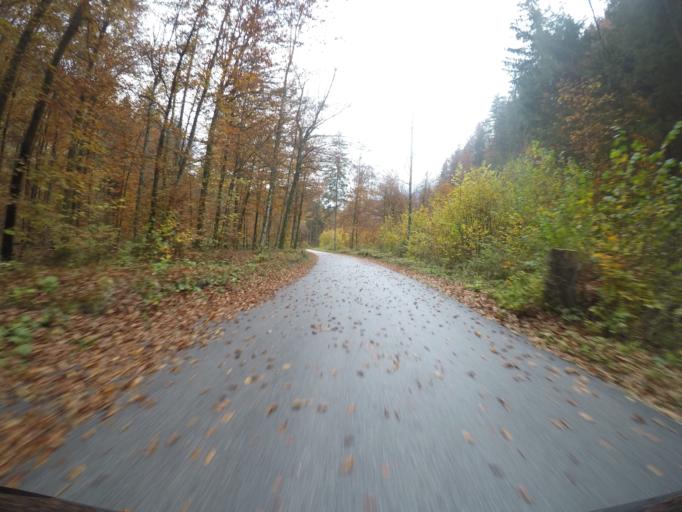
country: SI
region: Jesenice
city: Hrusica
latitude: 46.4274
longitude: 13.9699
